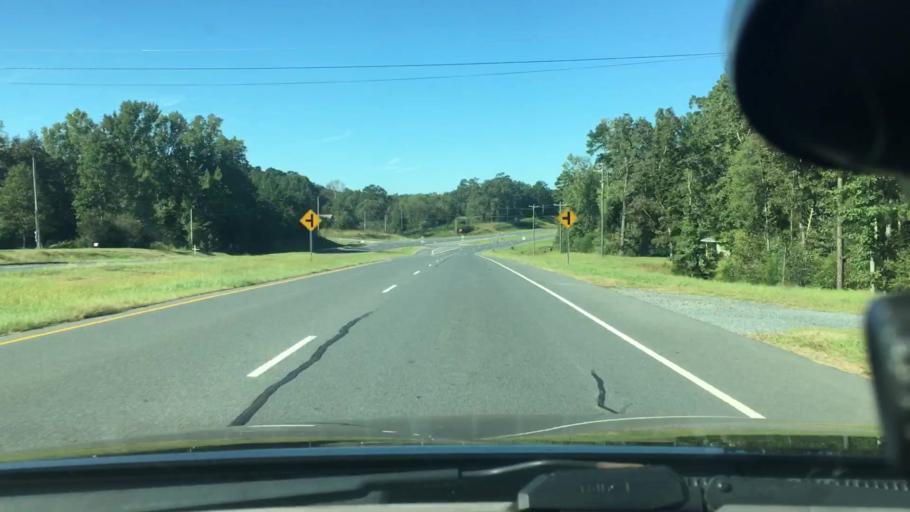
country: US
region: North Carolina
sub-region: Stanly County
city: Oakboro
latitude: 35.2702
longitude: -80.3327
